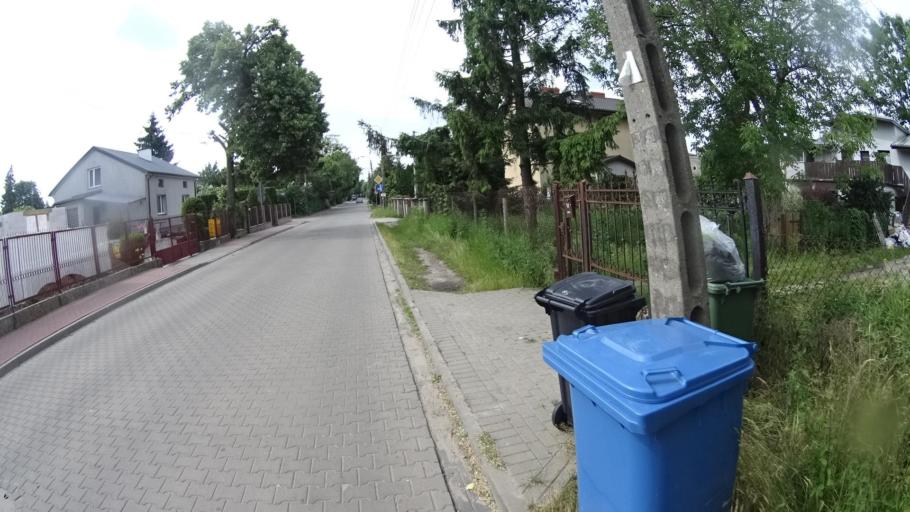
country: PL
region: Masovian Voivodeship
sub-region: Powiat pruszkowski
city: Piastow
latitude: 52.1927
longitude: 20.8521
